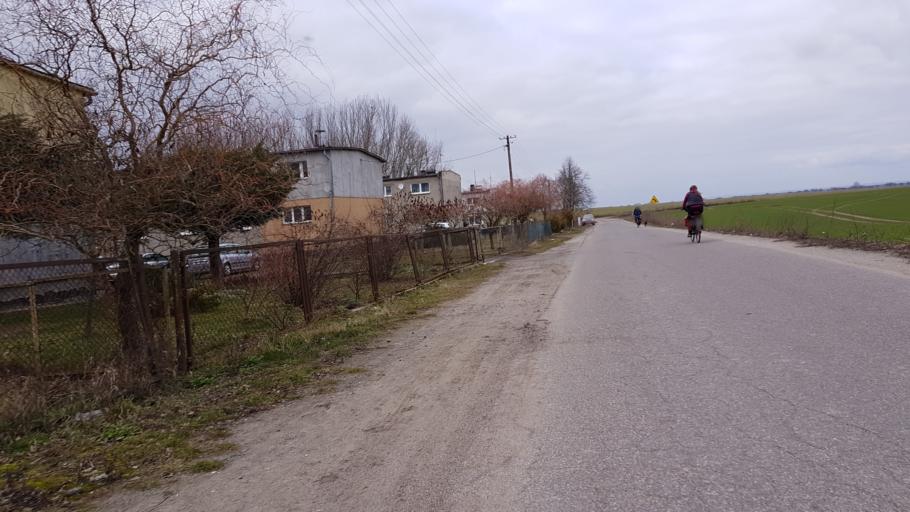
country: PL
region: West Pomeranian Voivodeship
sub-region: Powiat gryfinski
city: Banie
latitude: 53.0948
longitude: 14.7067
